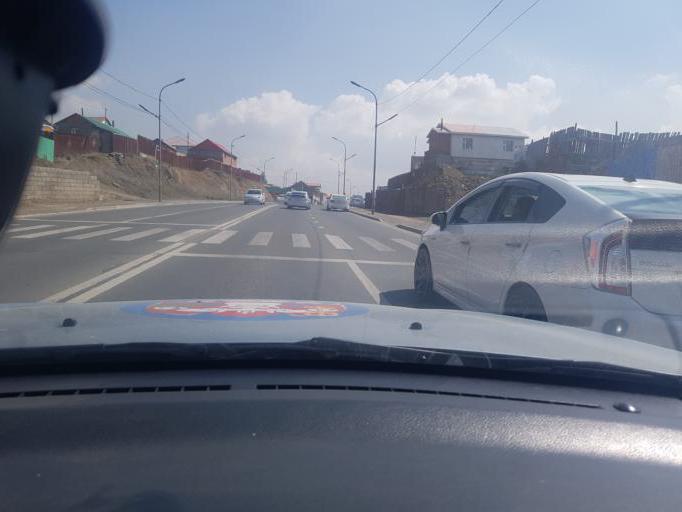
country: MN
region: Ulaanbaatar
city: Ulaanbaatar
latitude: 47.9556
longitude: 106.8467
